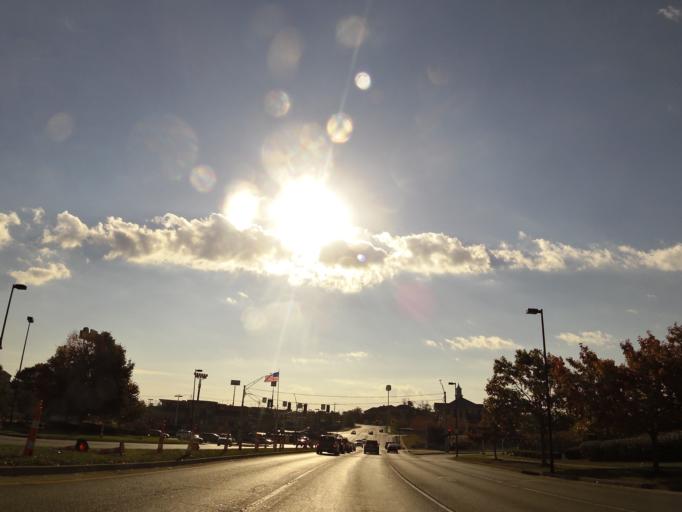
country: US
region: Kentucky
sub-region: Fayette County
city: Lexington-Fayette
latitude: 38.0200
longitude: -84.4177
